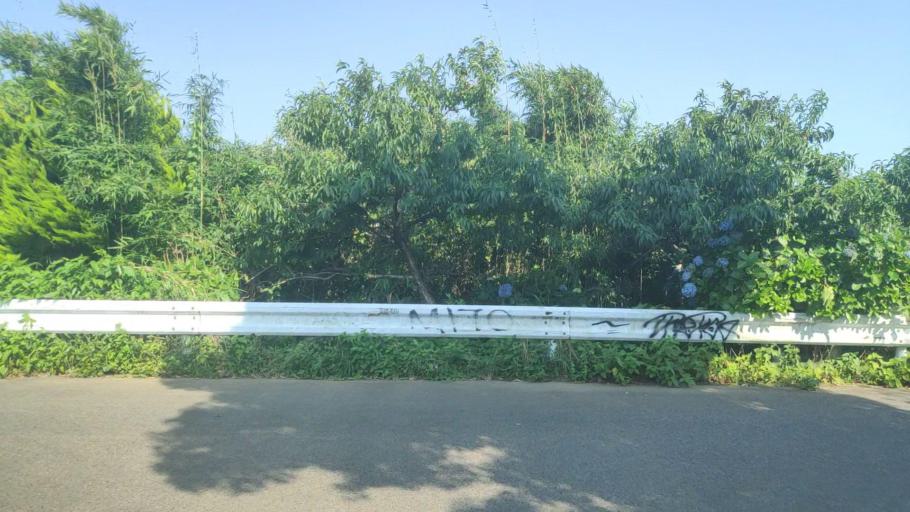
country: JP
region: Kanagawa
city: Hiratsuka
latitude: 35.3456
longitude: 139.3238
